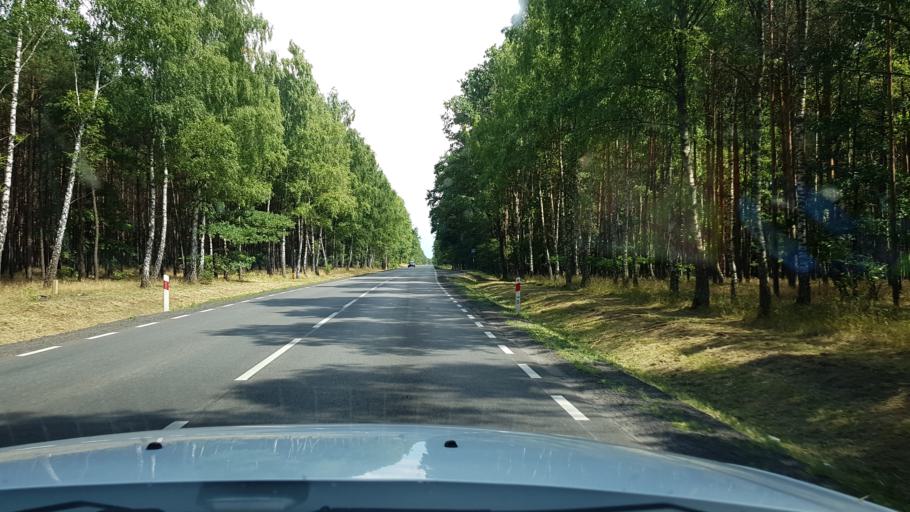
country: PL
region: West Pomeranian Voivodeship
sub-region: Powiat walecki
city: Walcz
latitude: 53.3114
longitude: 16.3722
